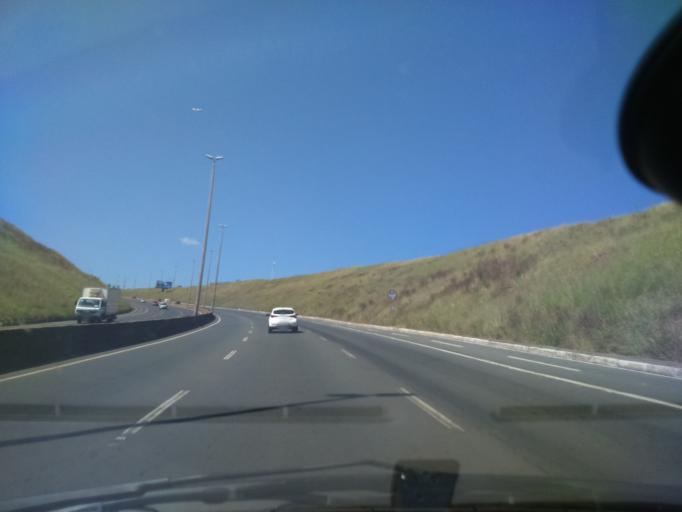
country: BR
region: Federal District
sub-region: Brasilia
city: Brasilia
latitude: -15.8378
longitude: -47.8250
